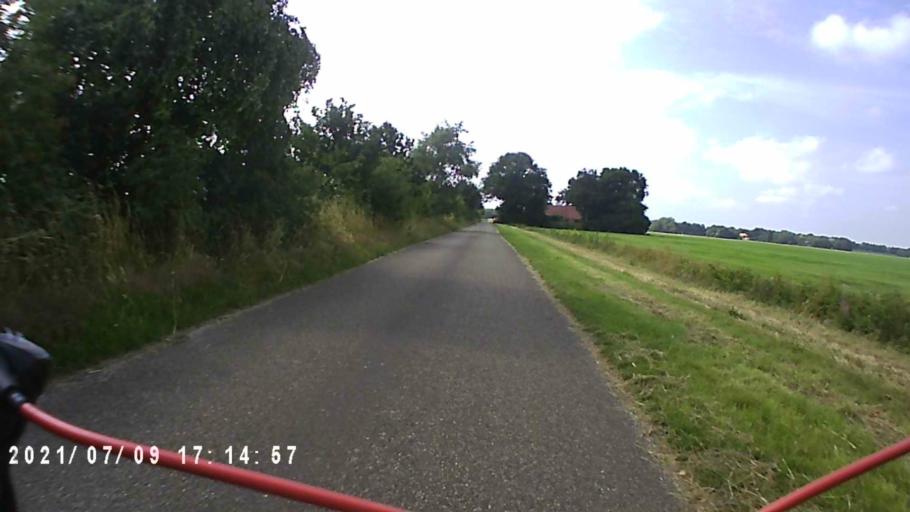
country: DE
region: Lower Saxony
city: Rhede
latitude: 53.0867
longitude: 7.1869
